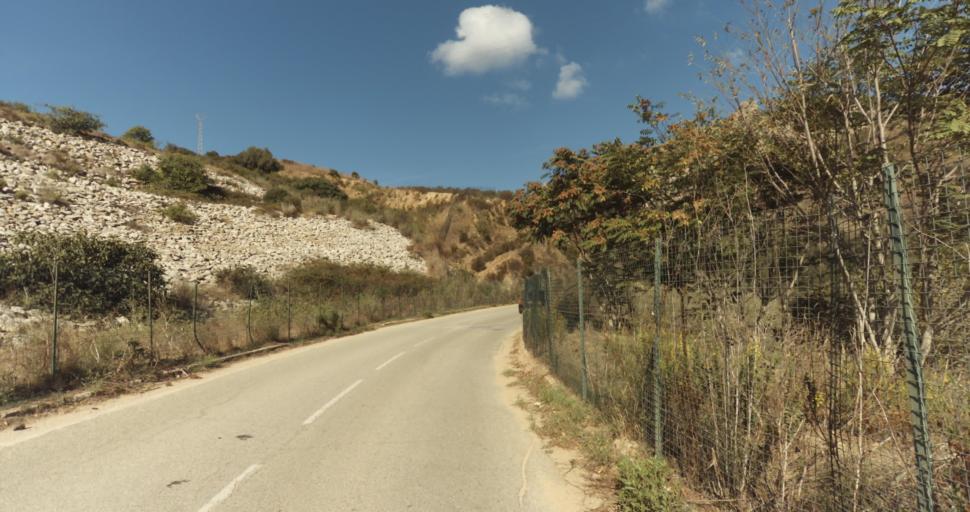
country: FR
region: Corsica
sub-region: Departement de la Corse-du-Sud
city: Ajaccio
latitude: 41.9322
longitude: 8.6907
